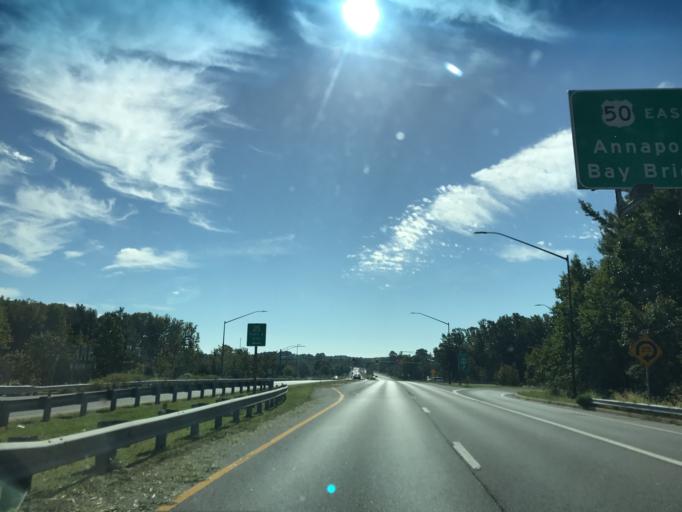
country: US
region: Maryland
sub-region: Anne Arundel County
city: Davidsonville
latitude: 38.9607
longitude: -76.6549
